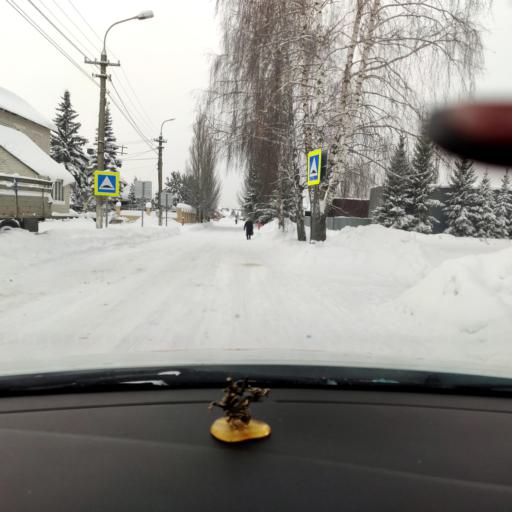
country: RU
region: Tatarstan
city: Stolbishchi
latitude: 55.6098
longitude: 49.1410
